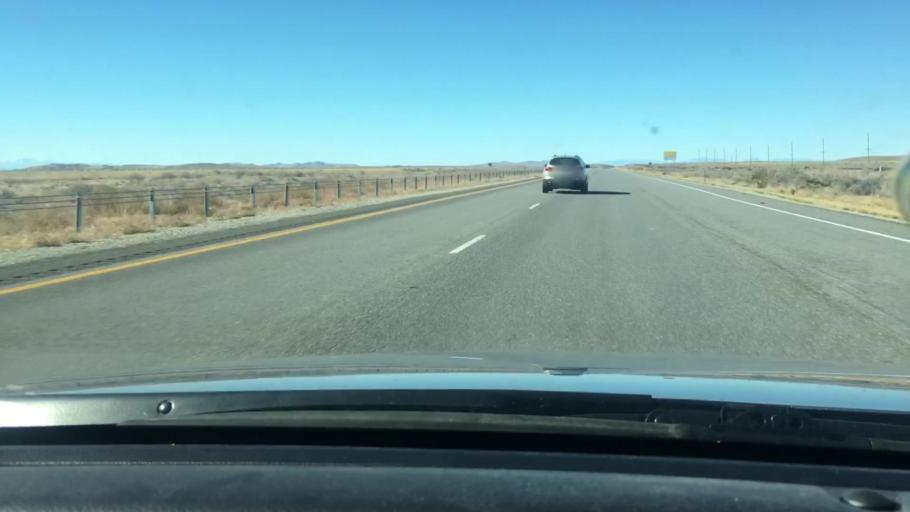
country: US
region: Utah
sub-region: Tooele County
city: Grantsville
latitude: 40.7305
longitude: -113.1213
